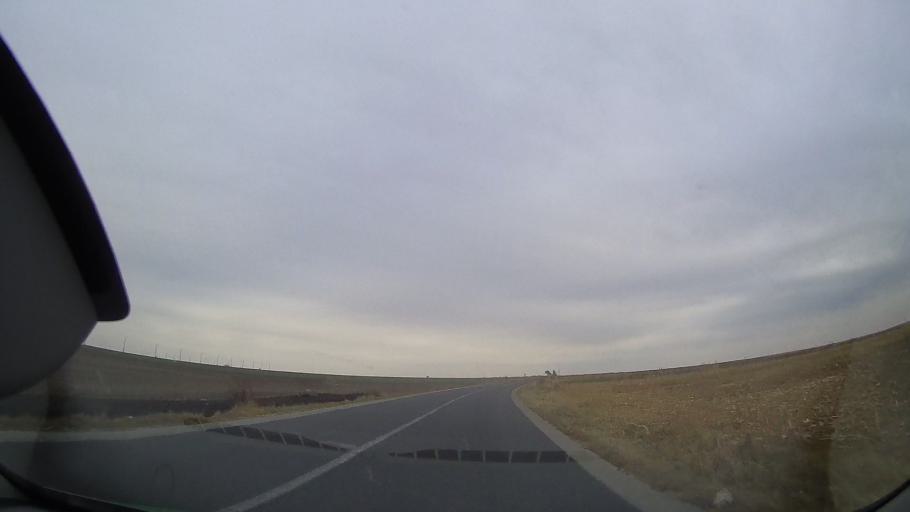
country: RO
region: Ialomita
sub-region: Comuna Milosesti
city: Milosesti
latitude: 44.7580
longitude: 27.2023
